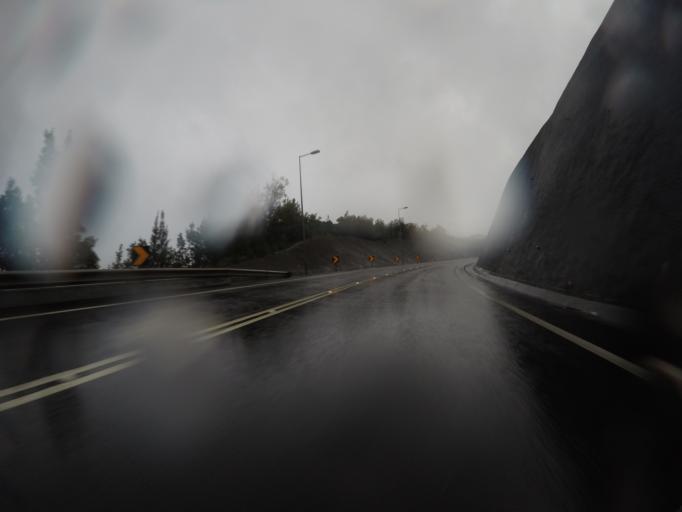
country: PT
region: Madeira
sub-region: Santana
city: Santana
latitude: 32.7635
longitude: -16.8322
